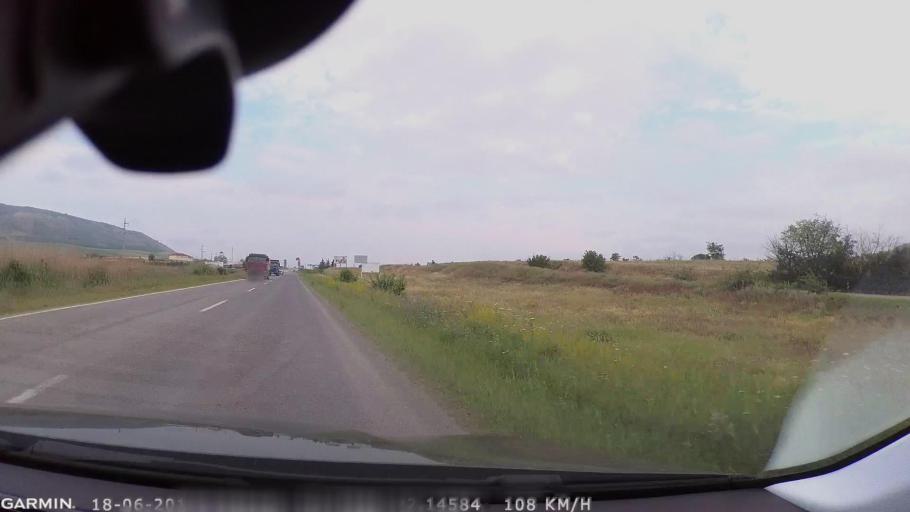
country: MK
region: Stip
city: Shtip
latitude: 41.7717
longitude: 22.1442
